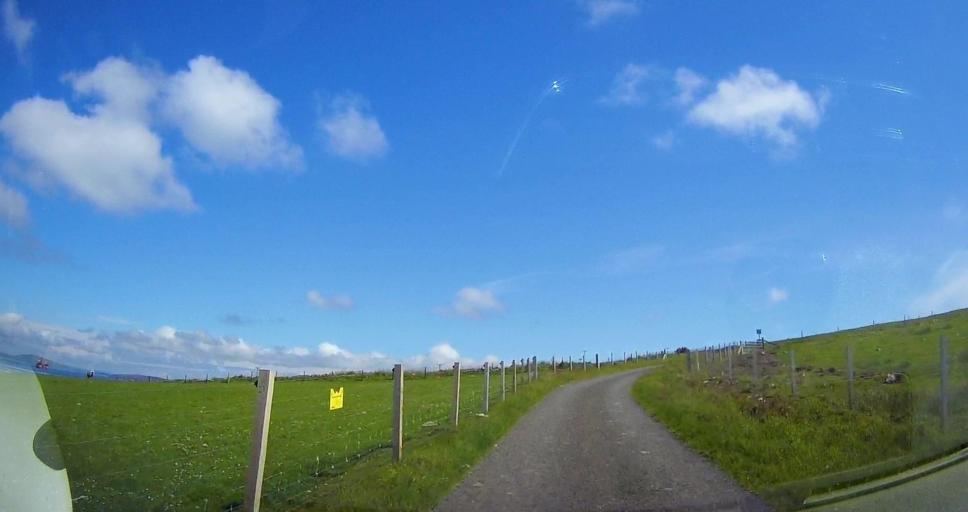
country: GB
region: Scotland
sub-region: Orkney Islands
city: Orkney
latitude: 58.8531
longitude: -2.9532
